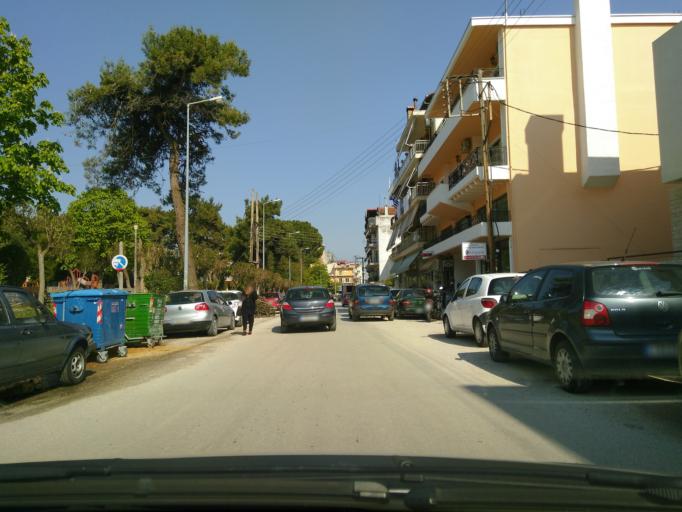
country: GR
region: Epirus
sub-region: Nomos Ioanninon
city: Ioannina
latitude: 39.6733
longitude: 20.8453
